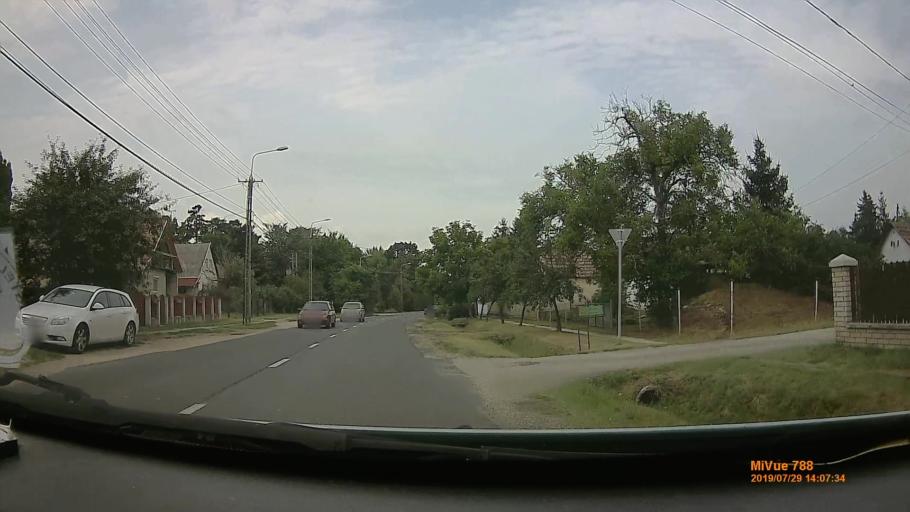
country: HU
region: Somogy
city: Balatonfoldvar
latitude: 46.8250
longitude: 17.9035
